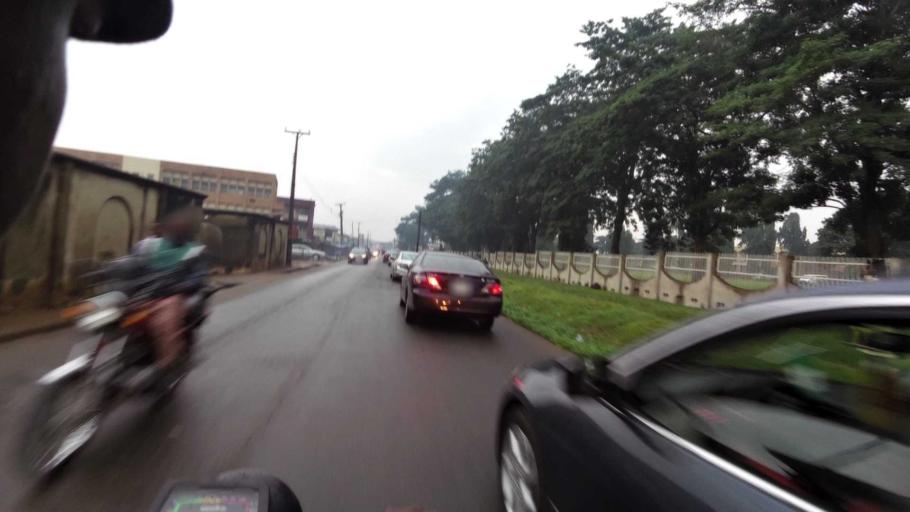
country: NG
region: Oyo
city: Ibadan
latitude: 7.4116
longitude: 3.9310
